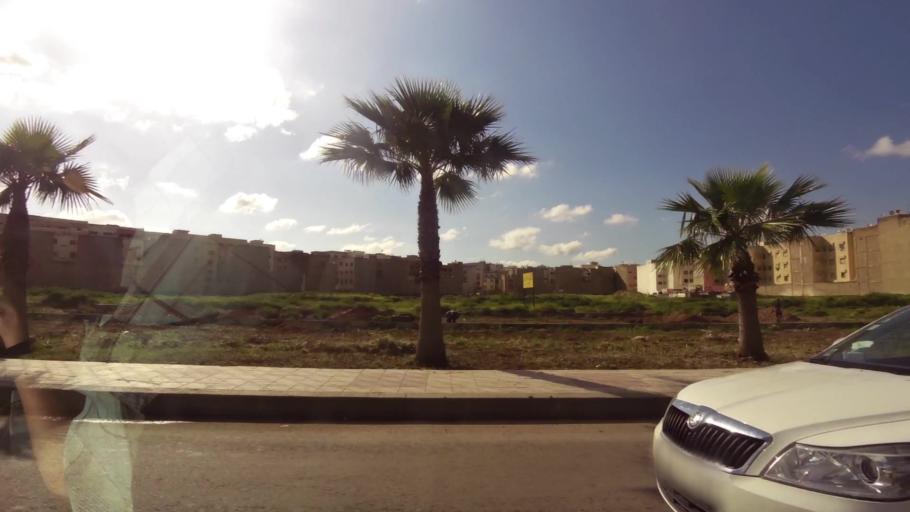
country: MA
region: Chaouia-Ouardigha
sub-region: Settat Province
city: Berrechid
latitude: 33.2729
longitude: -7.5845
